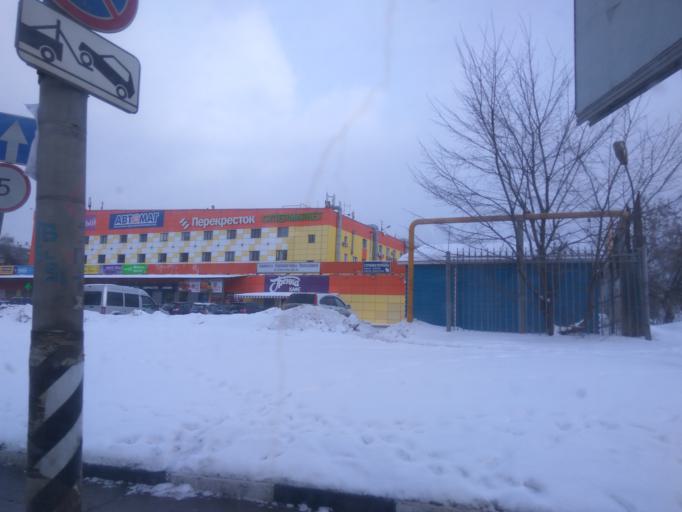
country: RU
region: Moscow
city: Likhobory
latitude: 55.8071
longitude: 37.5719
